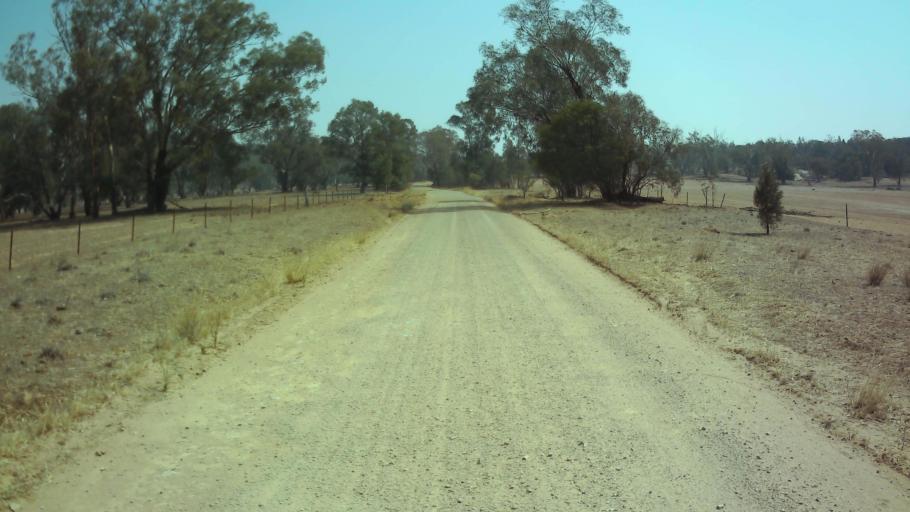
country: AU
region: New South Wales
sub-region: Weddin
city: Grenfell
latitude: -33.6677
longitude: 148.2747
